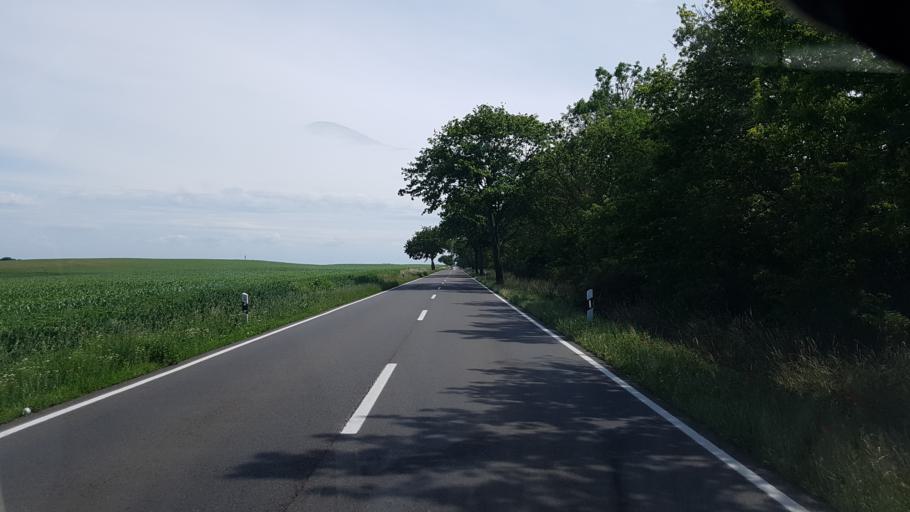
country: DE
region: Brandenburg
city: Prenzlau
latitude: 53.3765
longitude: 13.7838
